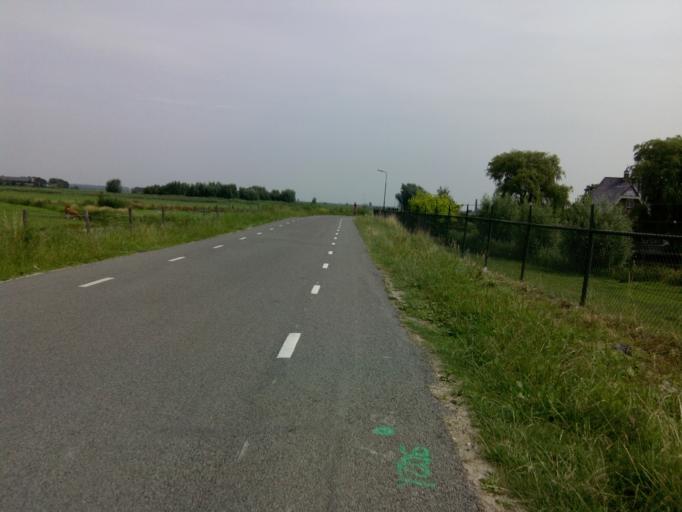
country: NL
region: Utrecht
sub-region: Gemeente Baarn
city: Baarn
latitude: 52.2493
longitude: 5.3171
